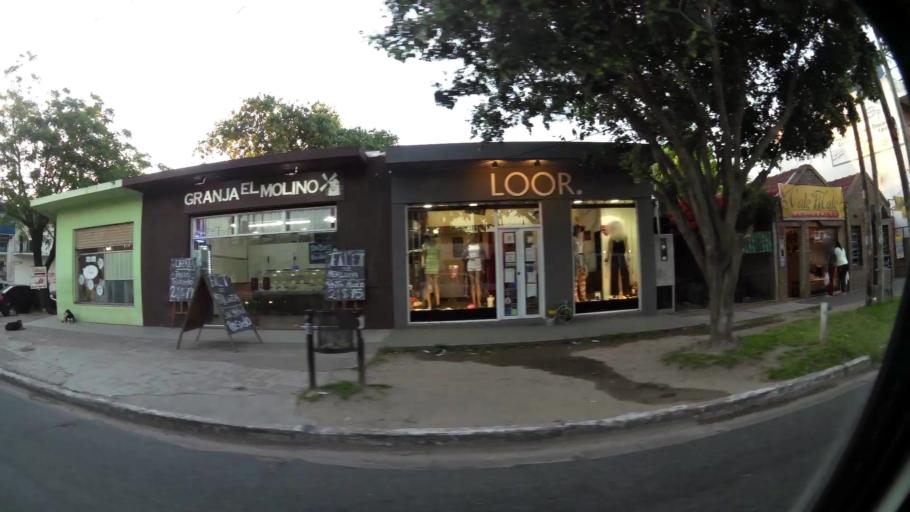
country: AR
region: Buenos Aires
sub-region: Partido de Quilmes
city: Quilmes
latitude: -34.8090
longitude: -58.1868
